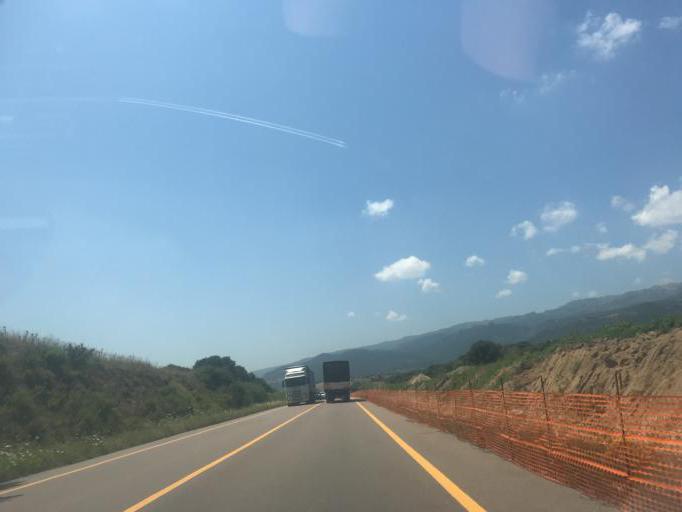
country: IT
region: Sardinia
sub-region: Provincia di Olbia-Tempio
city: Berchidda
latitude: 40.7803
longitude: 9.2262
